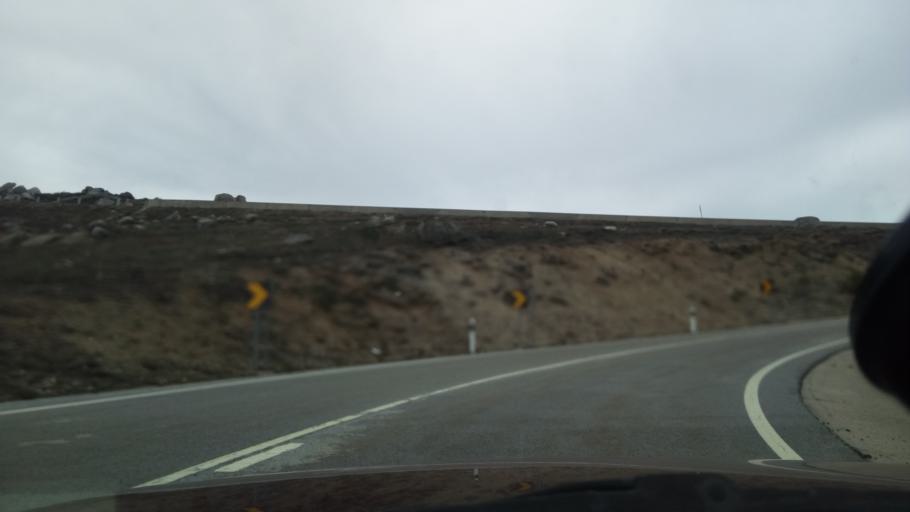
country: PT
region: Guarda
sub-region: Seia
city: Seia
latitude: 40.3448
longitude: -7.6980
